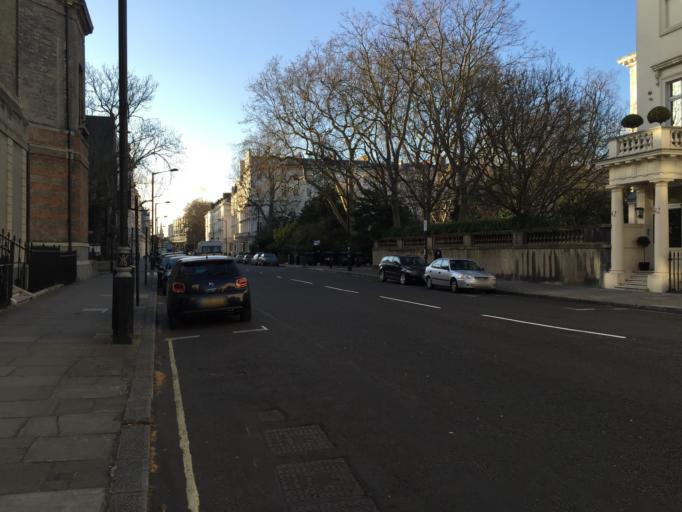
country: GB
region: England
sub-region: Greater London
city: Battersea
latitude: 51.4896
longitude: -0.1412
